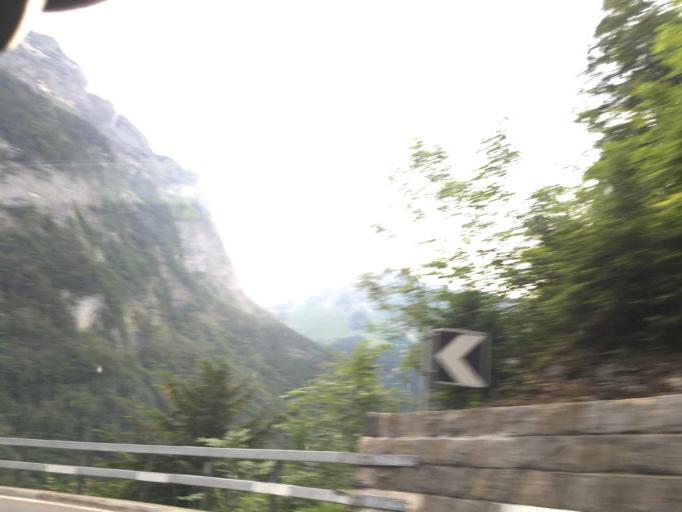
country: CH
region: Obwalden
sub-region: Obwalden
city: Engelberg
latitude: 46.8413
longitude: 8.3771
